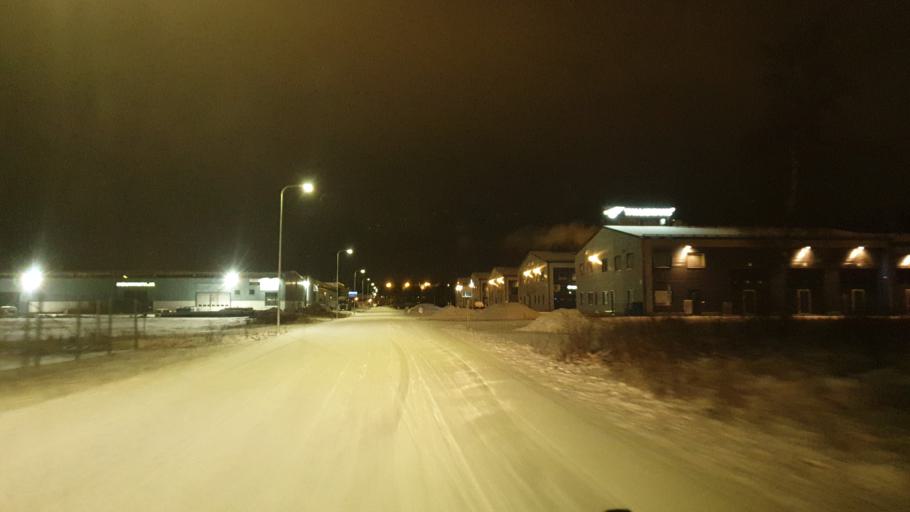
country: FI
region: Northern Ostrobothnia
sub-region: Oulu
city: Oulu
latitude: 64.9939
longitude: 25.4474
